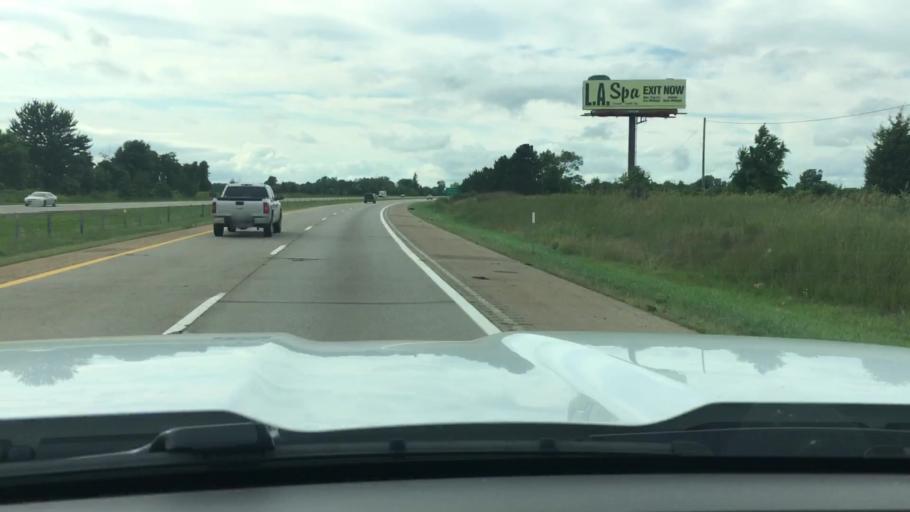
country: US
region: Michigan
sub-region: Ionia County
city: Portland
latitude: 42.8670
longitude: -84.9561
